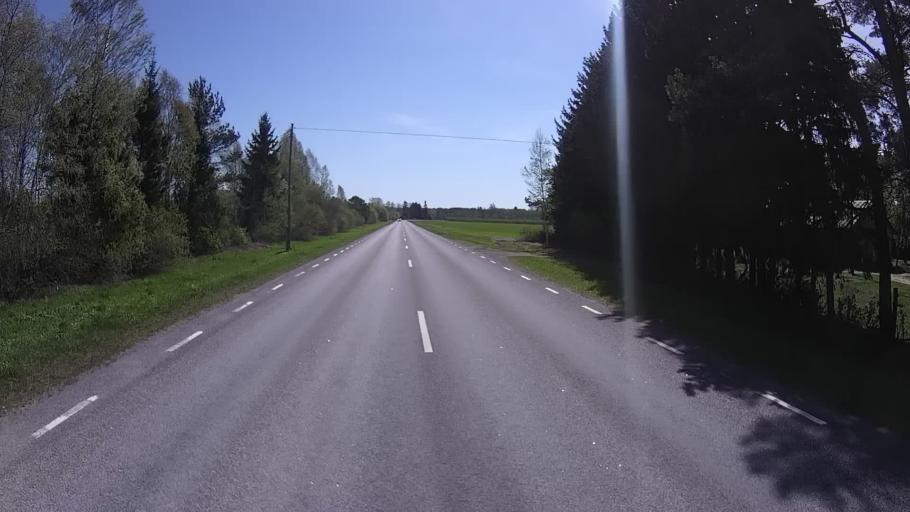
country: EE
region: Laeaene
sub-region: Ridala Parish
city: Uuemoisa
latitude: 58.8599
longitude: 23.6298
